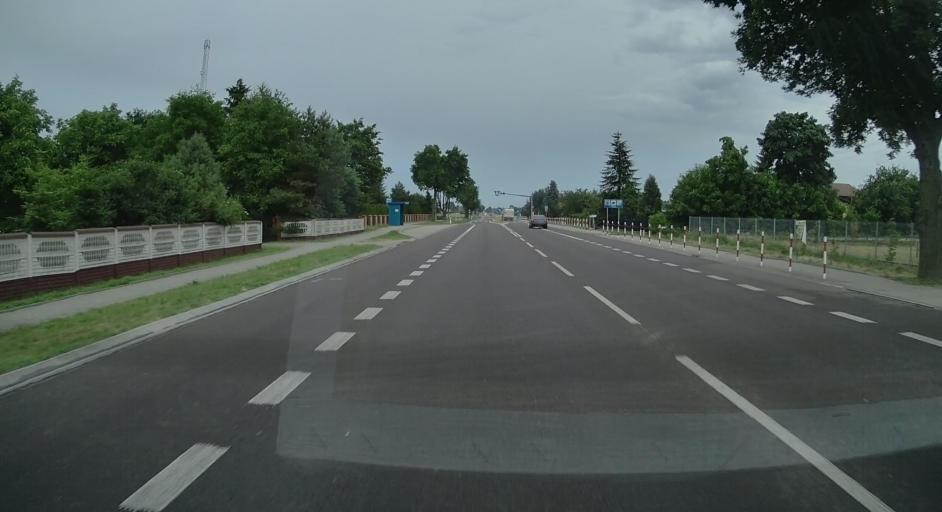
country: PL
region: Lublin Voivodeship
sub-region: Powiat bialski
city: Rzeczyca
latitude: 52.0273
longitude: 22.7117
